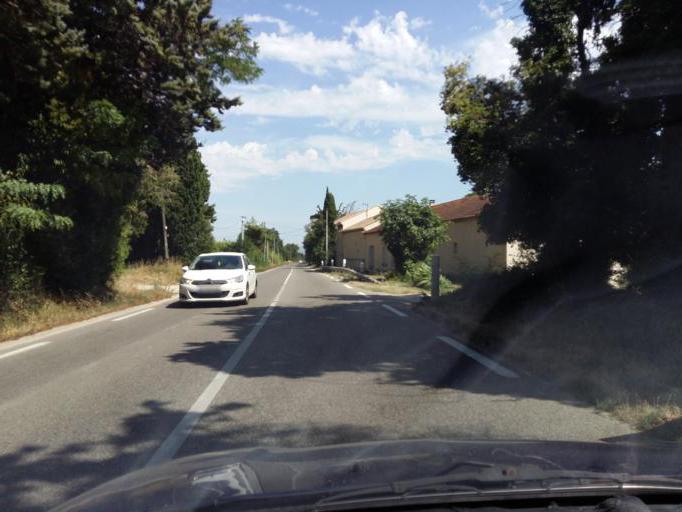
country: FR
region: Provence-Alpes-Cote d'Azur
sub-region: Departement du Vaucluse
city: Jonquieres
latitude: 44.1027
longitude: 4.9296
